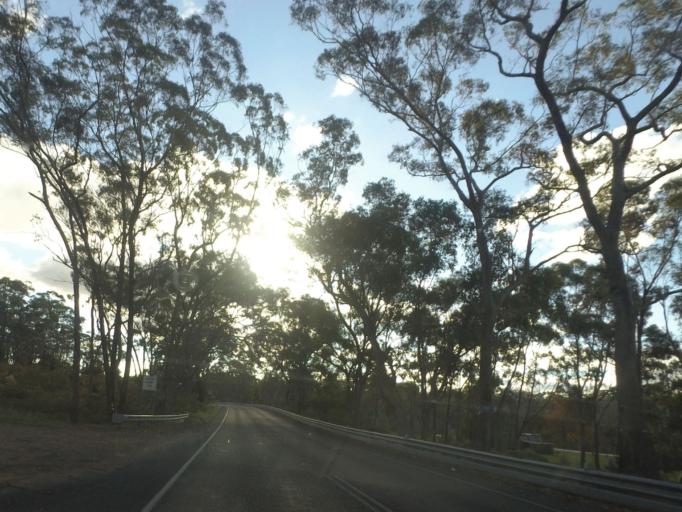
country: AU
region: Victoria
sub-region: Mount Alexander
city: Castlemaine
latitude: -37.0867
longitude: 144.2790
